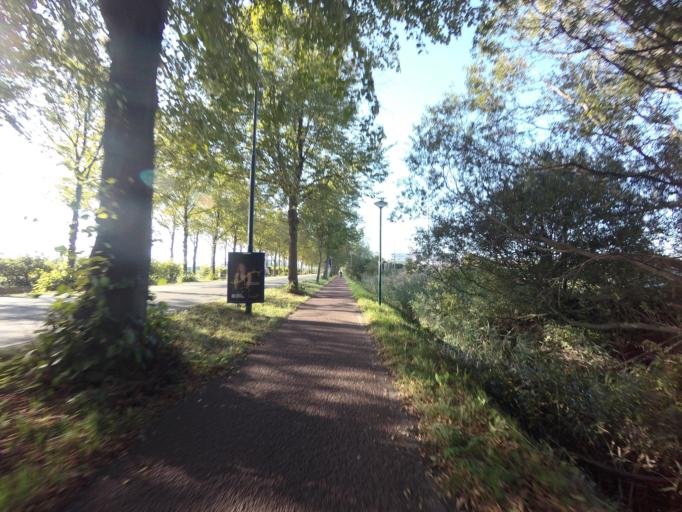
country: NL
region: Utrecht
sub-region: Stichtse Vecht
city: Maarssen
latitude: 52.1235
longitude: 5.0606
